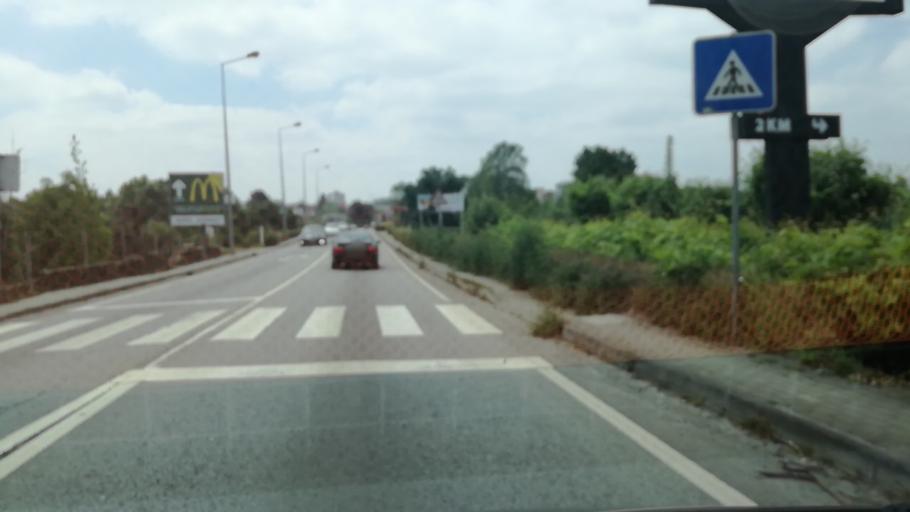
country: PT
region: Braga
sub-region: Vila Nova de Famalicao
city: Ferreiros
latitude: 41.3468
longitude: -8.5562
